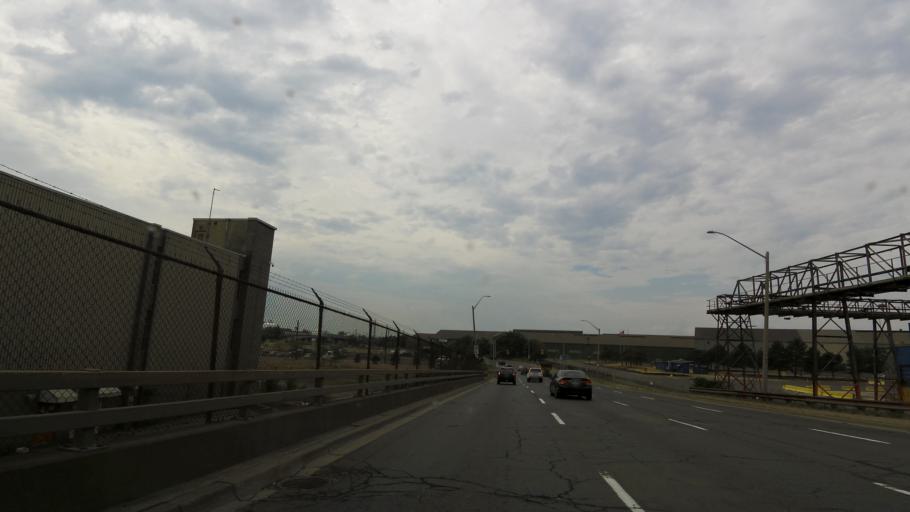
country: CA
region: Ontario
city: Hamilton
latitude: 43.2644
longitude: -79.8198
